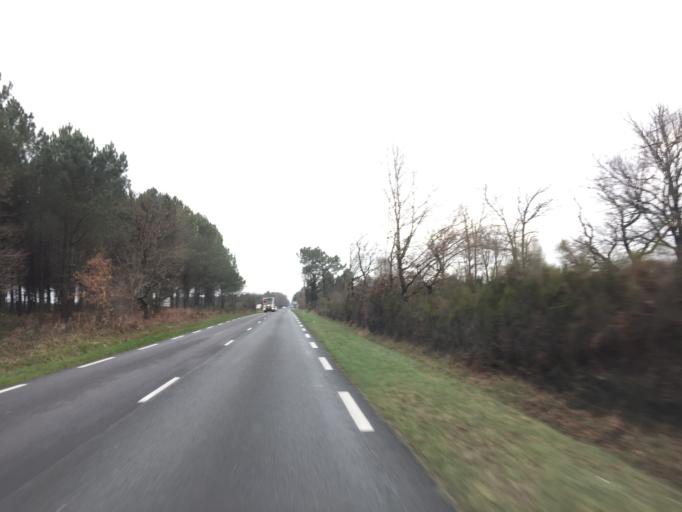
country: FR
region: Aquitaine
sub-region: Departement de la Gironde
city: Saint-Sauveur
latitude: 45.1809
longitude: -0.8437
